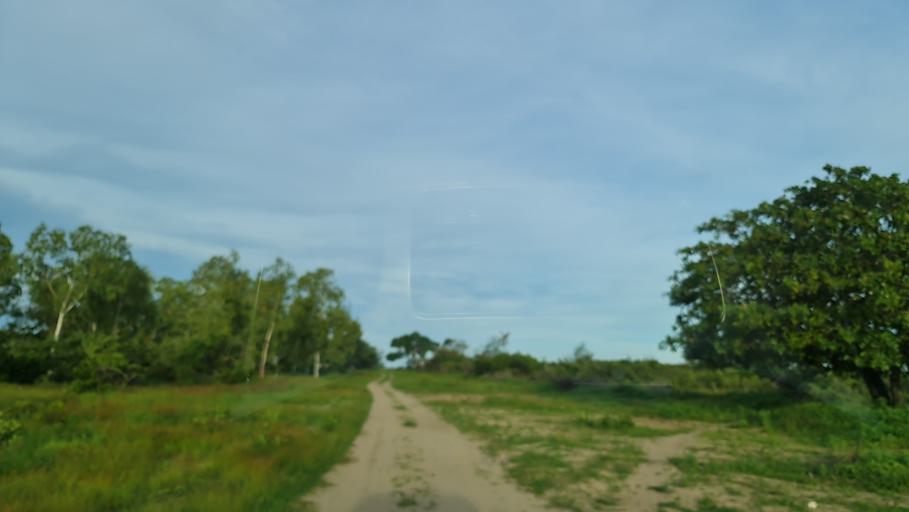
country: MZ
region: Nampula
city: Nacala
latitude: -14.7781
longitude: 40.8199
